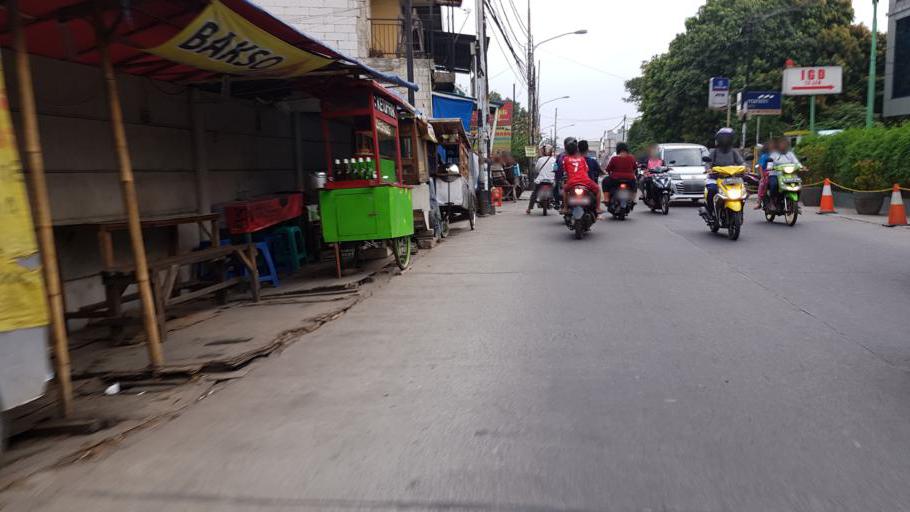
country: ID
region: West Java
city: Bekasi
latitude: -6.2820
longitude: 106.9305
